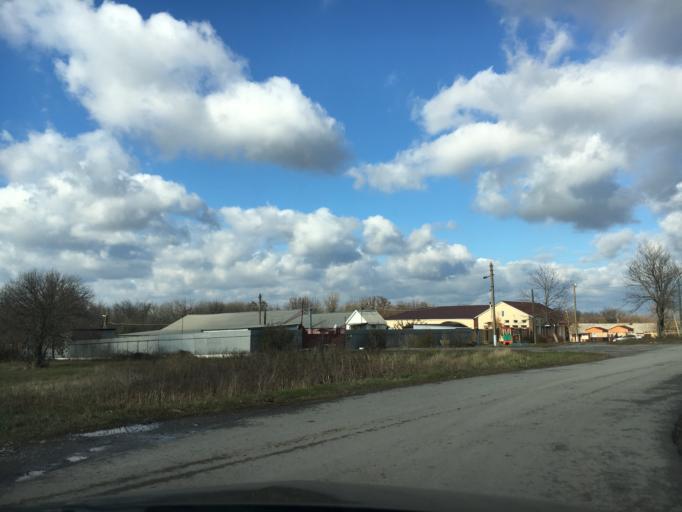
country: RU
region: Rostov
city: Pokrovskoye
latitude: 47.4810
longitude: 38.9149
